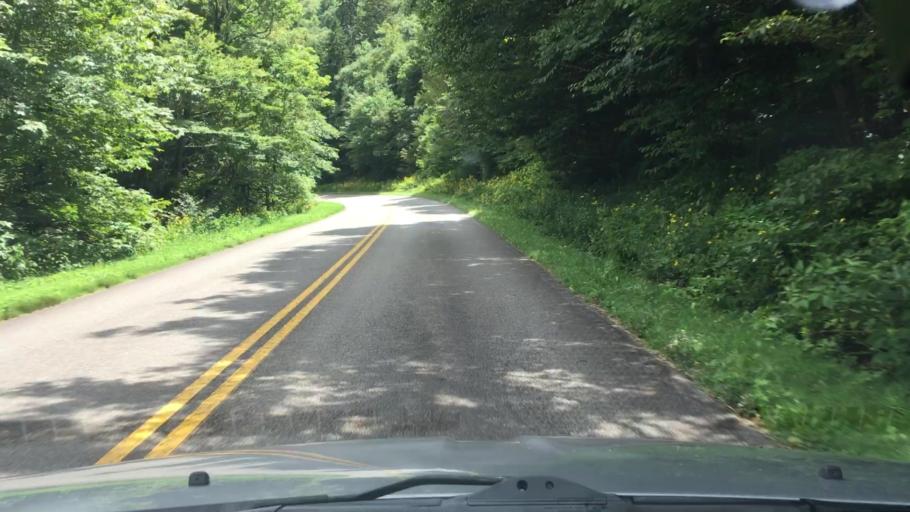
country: US
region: North Carolina
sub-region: Buncombe County
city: Black Mountain
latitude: 35.7096
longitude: -82.2740
